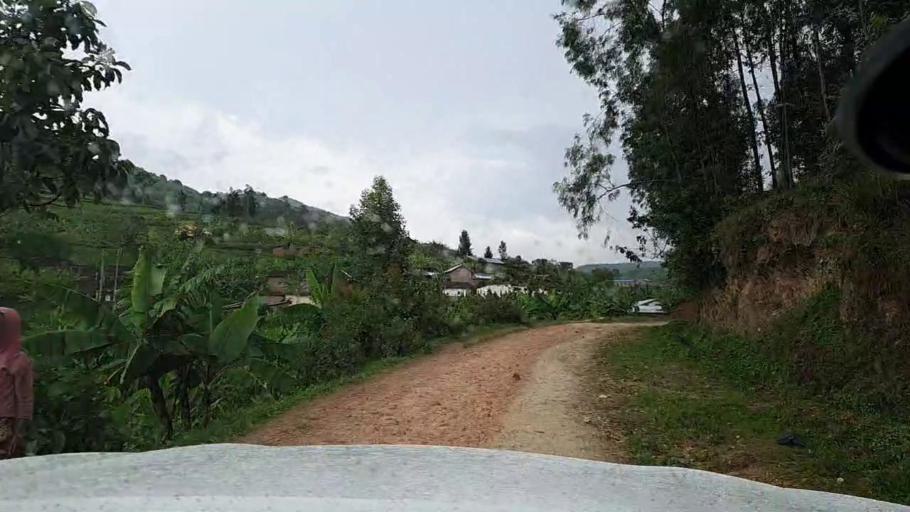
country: RW
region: Western Province
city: Kibuye
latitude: -2.0769
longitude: 29.4407
